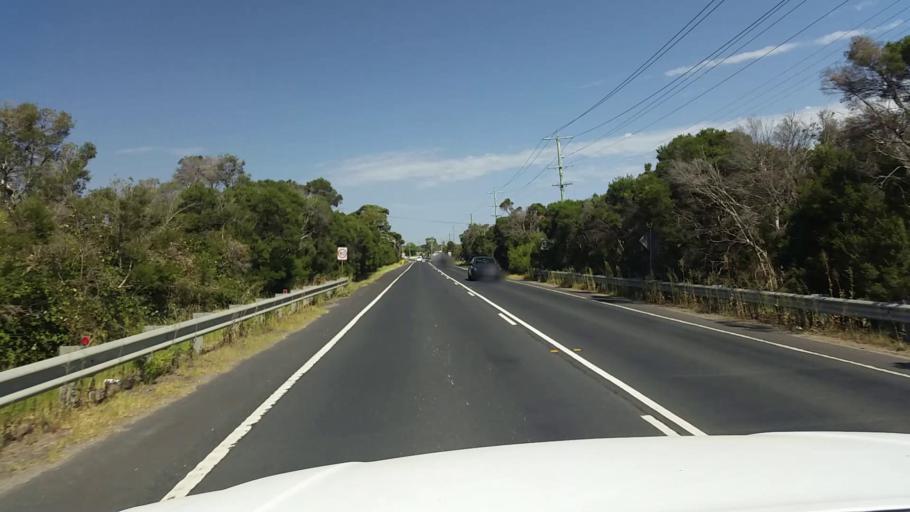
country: AU
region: Victoria
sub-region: Mornington Peninsula
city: Tyabb
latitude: -38.2518
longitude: 145.1906
